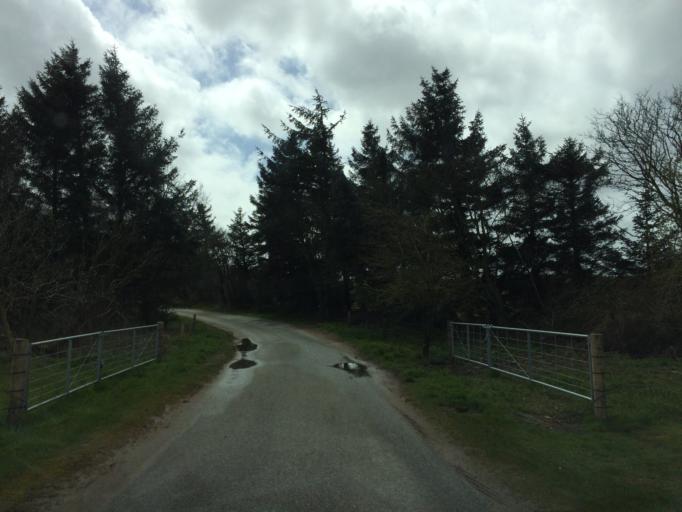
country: DK
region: South Denmark
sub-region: Varde Kommune
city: Oksbol
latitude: 55.5708
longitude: 8.3089
